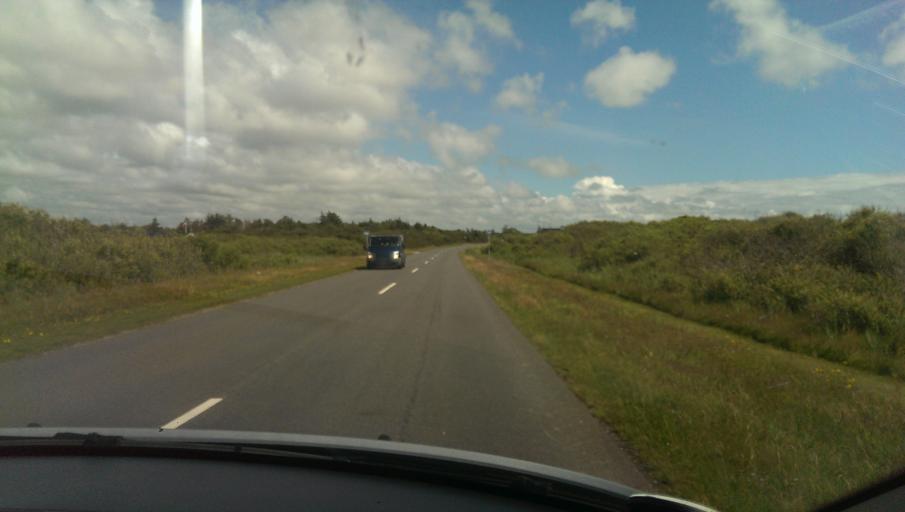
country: DK
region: Central Jutland
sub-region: Ringkobing-Skjern Kommune
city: Ringkobing
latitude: 56.1456
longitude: 8.1311
